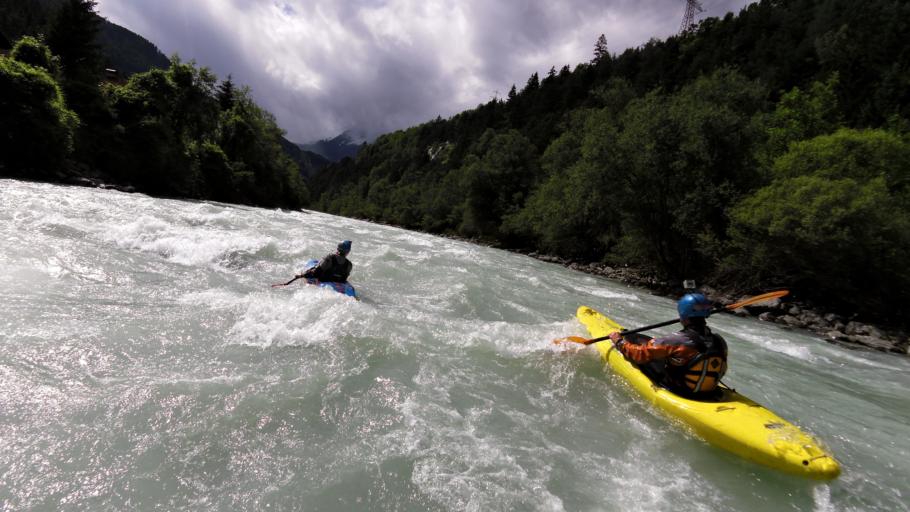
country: AT
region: Tyrol
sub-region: Politischer Bezirk Landeck
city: Landeck
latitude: 47.1227
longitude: 10.5975
